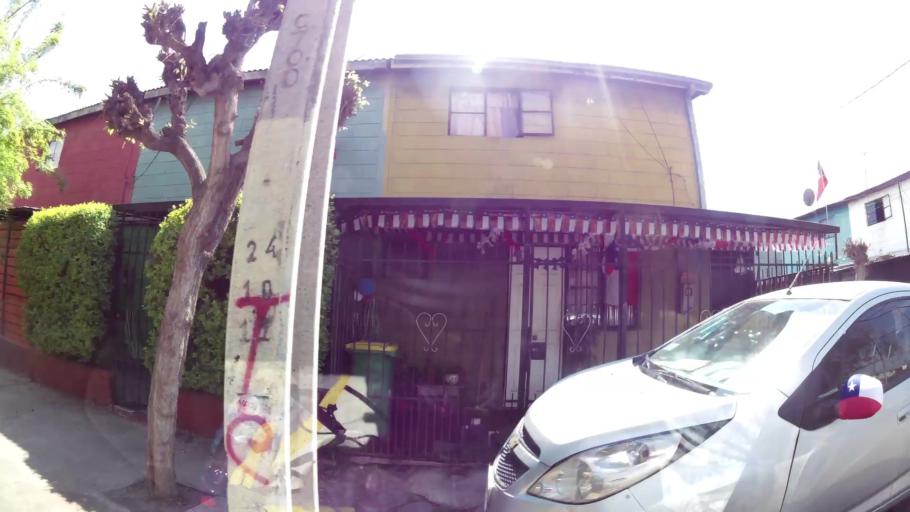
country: CL
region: Santiago Metropolitan
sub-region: Provincia de Santiago
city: La Pintana
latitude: -33.5602
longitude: -70.6353
